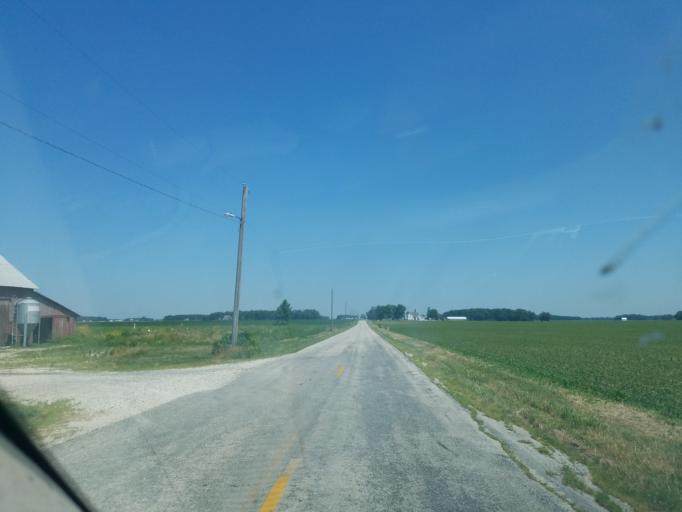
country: US
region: Ohio
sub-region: Mercer County
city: Coldwater
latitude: 40.5755
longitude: -84.7084
